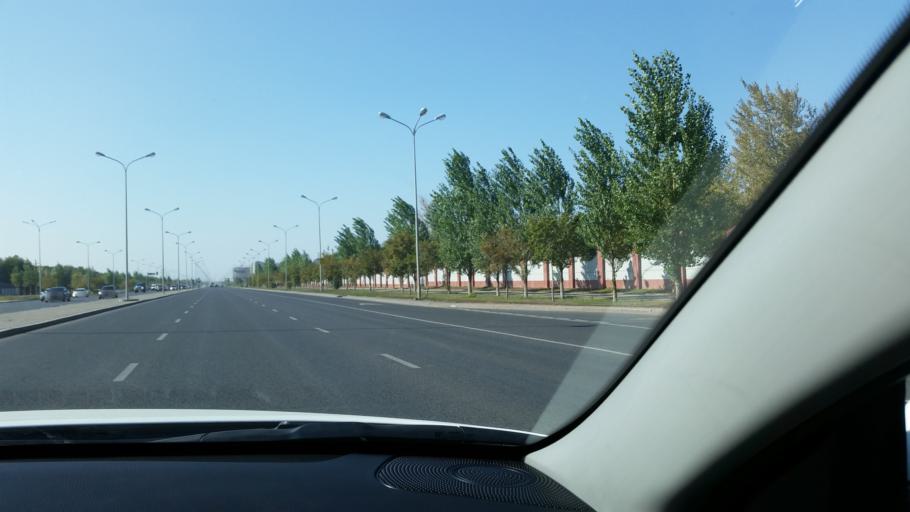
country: KZ
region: Astana Qalasy
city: Astana
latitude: 51.1843
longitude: 71.3630
